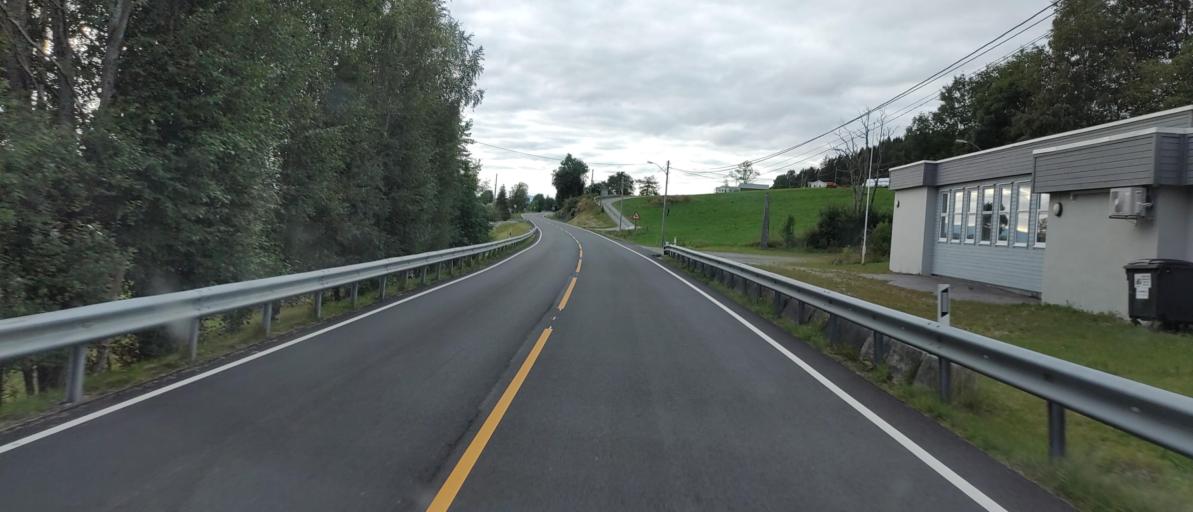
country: NO
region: More og Romsdal
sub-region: Molde
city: Hjelset
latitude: 62.6334
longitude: 7.5176
